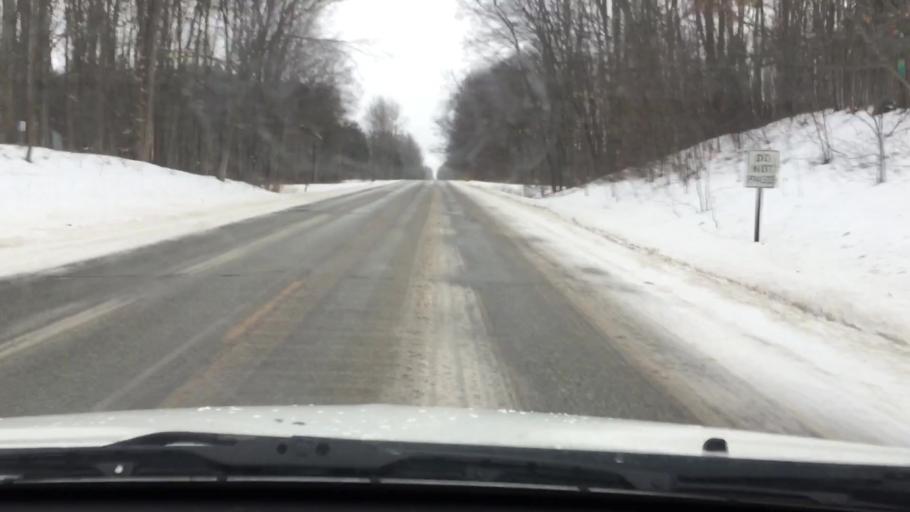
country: US
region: Michigan
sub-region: Wexford County
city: Cadillac
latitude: 44.1973
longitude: -85.4057
